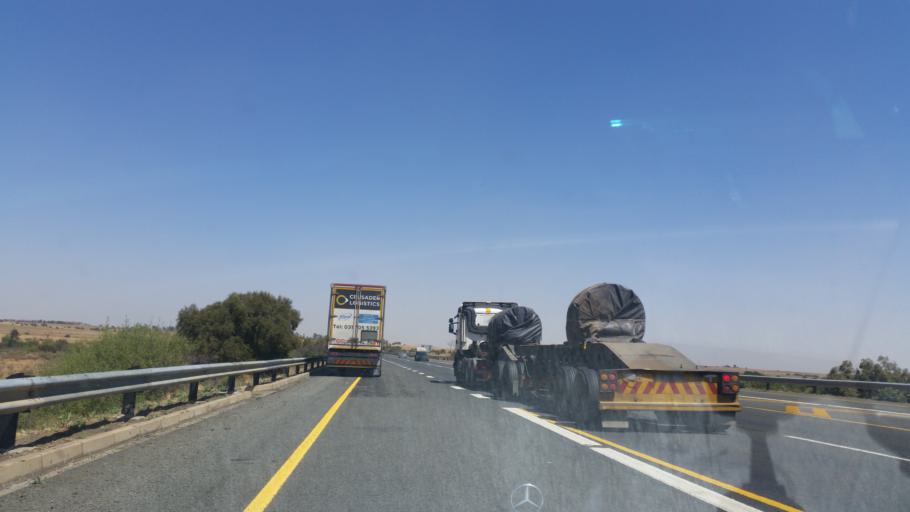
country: ZA
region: Orange Free State
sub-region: Lejweleputswa District Municipality
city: Winburg
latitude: -28.6298
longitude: 26.9064
